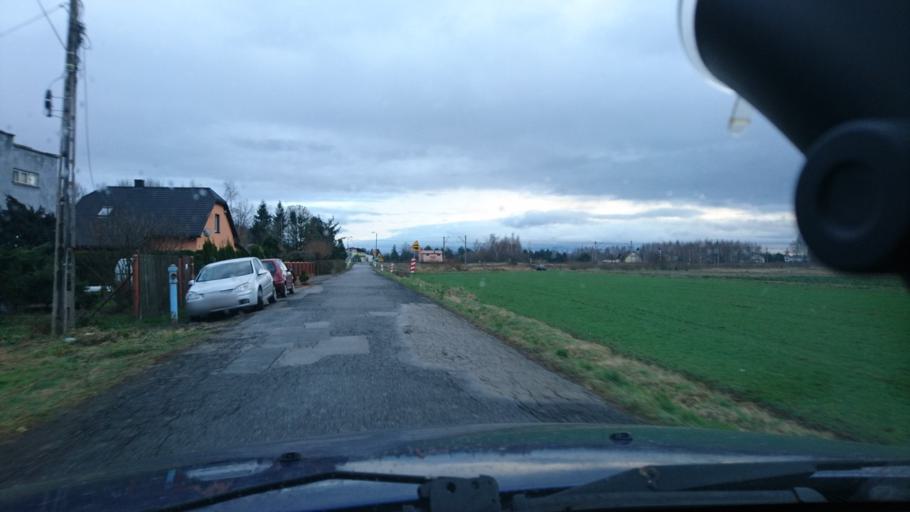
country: PL
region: Silesian Voivodeship
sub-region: Powiat bielski
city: Bestwinka
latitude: 49.9326
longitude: 19.0663
